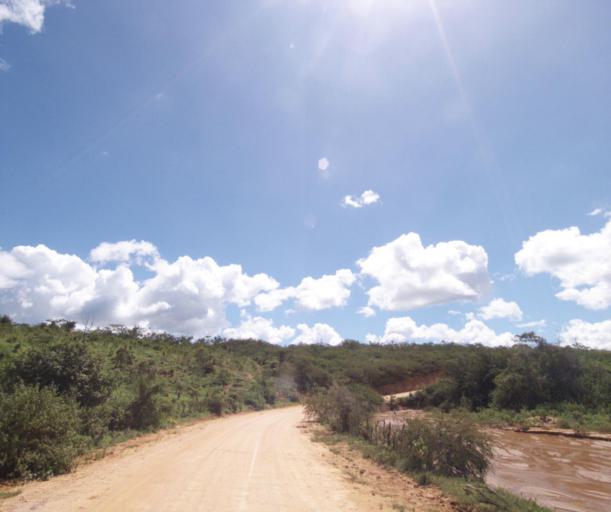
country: BR
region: Bahia
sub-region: Pocoes
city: Pocoes
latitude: -14.2995
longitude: -40.6413
